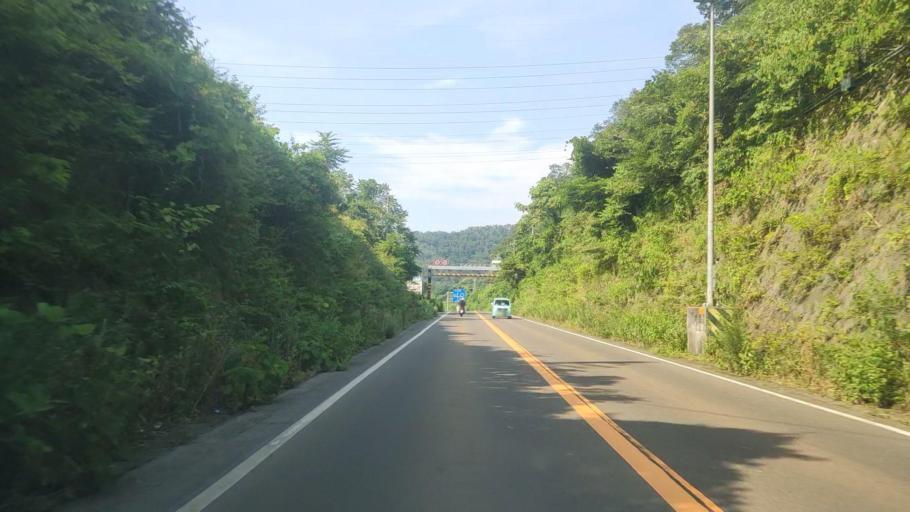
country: JP
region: Fukui
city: Tsuruga
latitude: 35.6711
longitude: 136.0859
